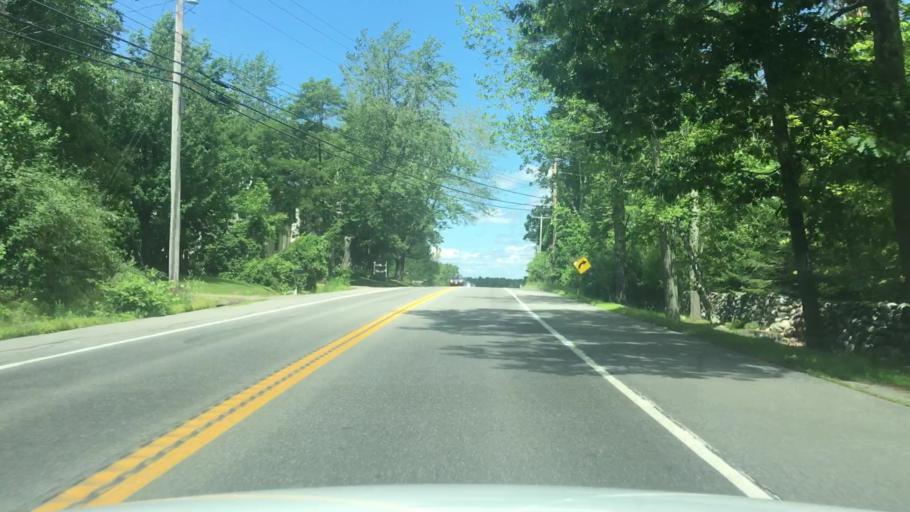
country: US
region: Maine
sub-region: Waldo County
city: Belfast
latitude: 44.3881
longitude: -68.9894
